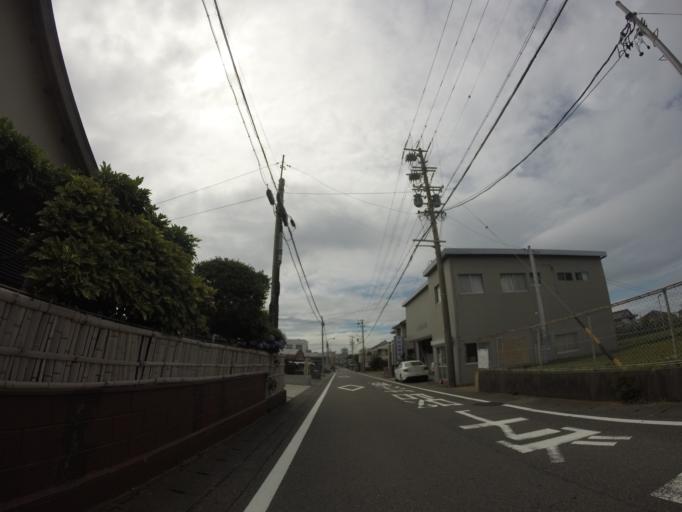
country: JP
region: Shizuoka
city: Oyama
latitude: 34.6087
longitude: 138.2098
